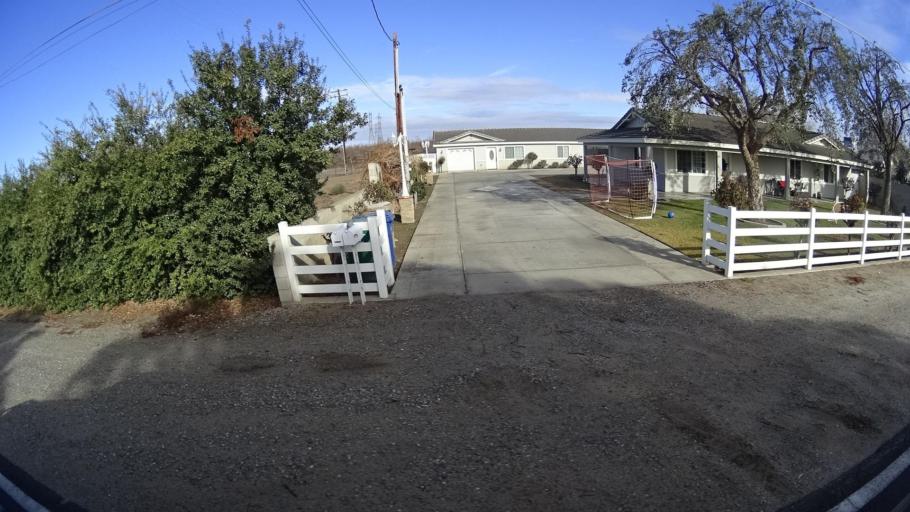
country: US
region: California
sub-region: Kern County
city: Rosedale
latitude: 35.3835
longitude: -119.2100
